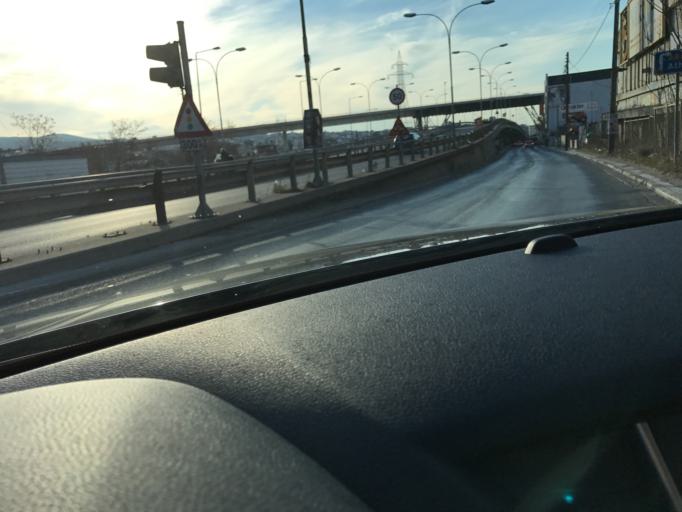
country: GR
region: Central Macedonia
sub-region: Nomos Thessalonikis
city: Stavroupoli
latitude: 40.6790
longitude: 22.9386
